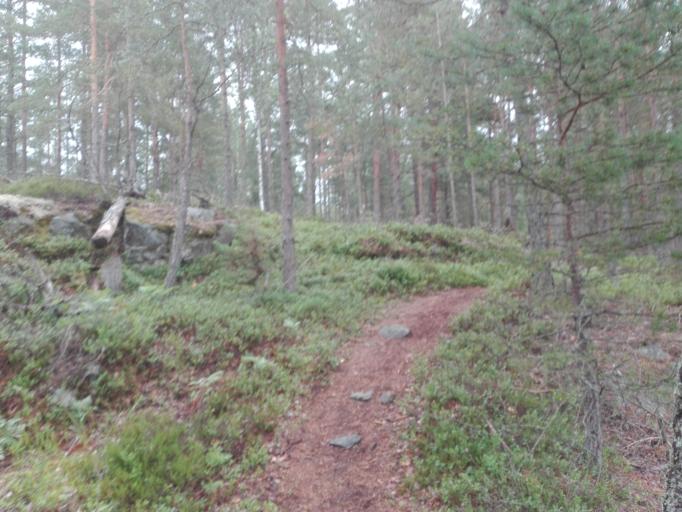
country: SE
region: Stockholm
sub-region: Nacka Kommun
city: Fisksatra
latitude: 59.2782
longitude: 18.2513
